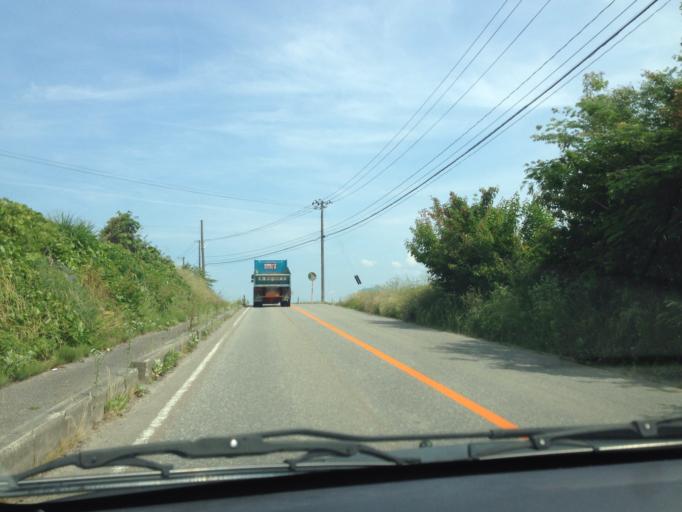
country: JP
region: Fukushima
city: Kitakata
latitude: 37.6063
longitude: 139.8062
